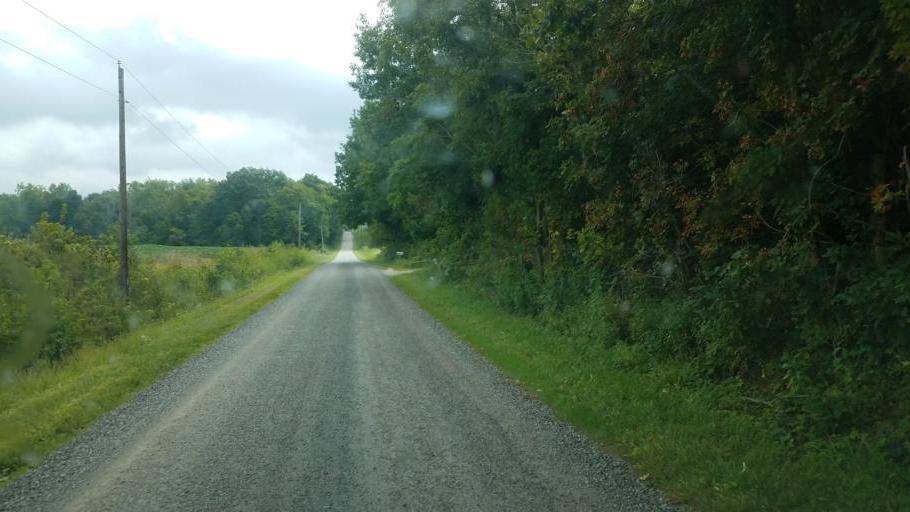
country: US
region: Ohio
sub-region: Morrow County
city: Mount Gilead
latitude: 40.4893
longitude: -82.7456
